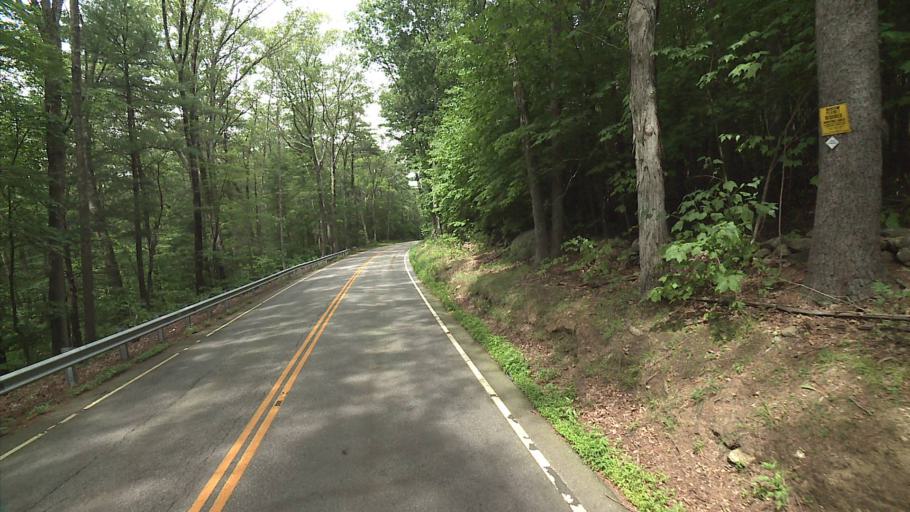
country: US
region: Massachusetts
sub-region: Hampden County
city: Holland
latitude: 41.9680
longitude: -72.1121
